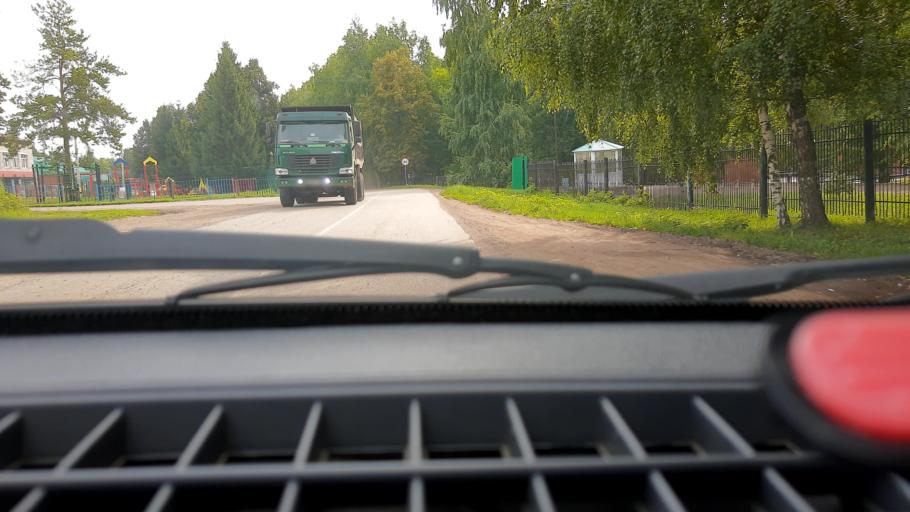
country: RU
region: Bashkortostan
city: Avdon
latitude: 54.6149
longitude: 55.6348
